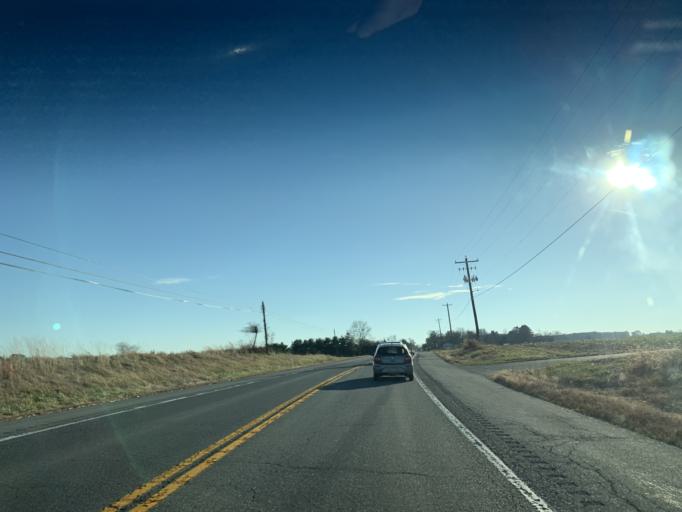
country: US
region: Delaware
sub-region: New Castle County
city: Middletown
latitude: 39.4160
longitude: -75.8616
